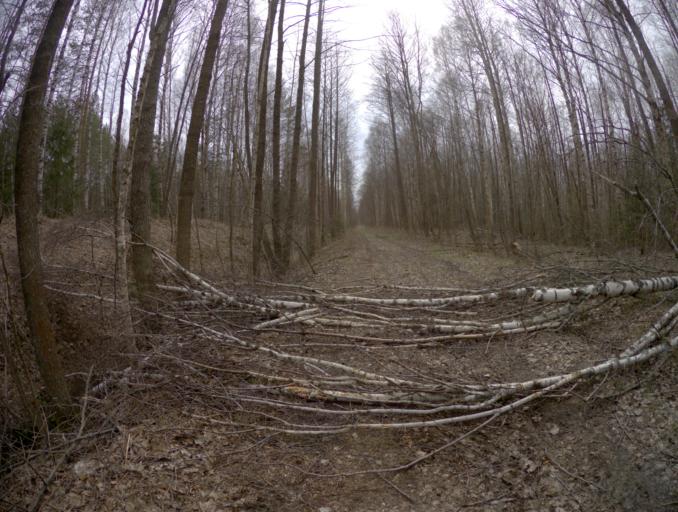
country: RU
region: Vladimir
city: Raduzhnyy
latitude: 55.9206
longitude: 40.2449
